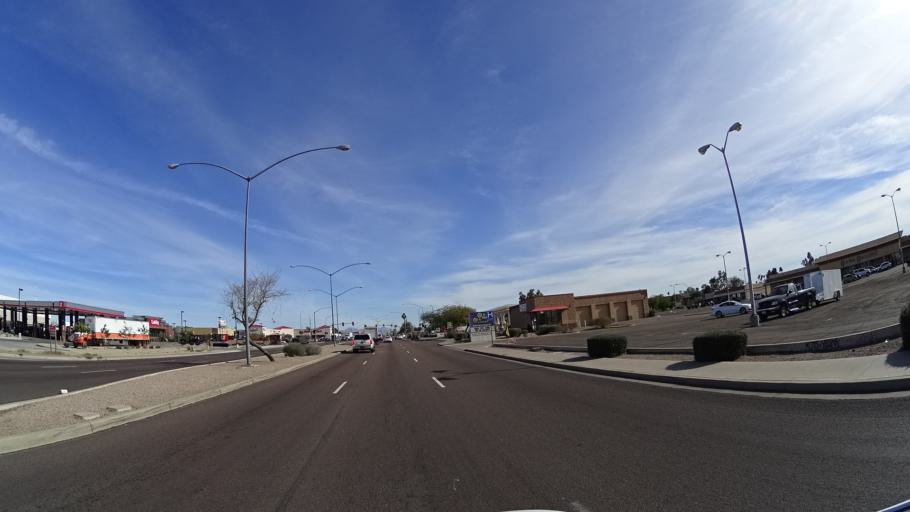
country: US
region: Arizona
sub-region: Maricopa County
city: Tempe
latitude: 33.4075
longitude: -111.8765
